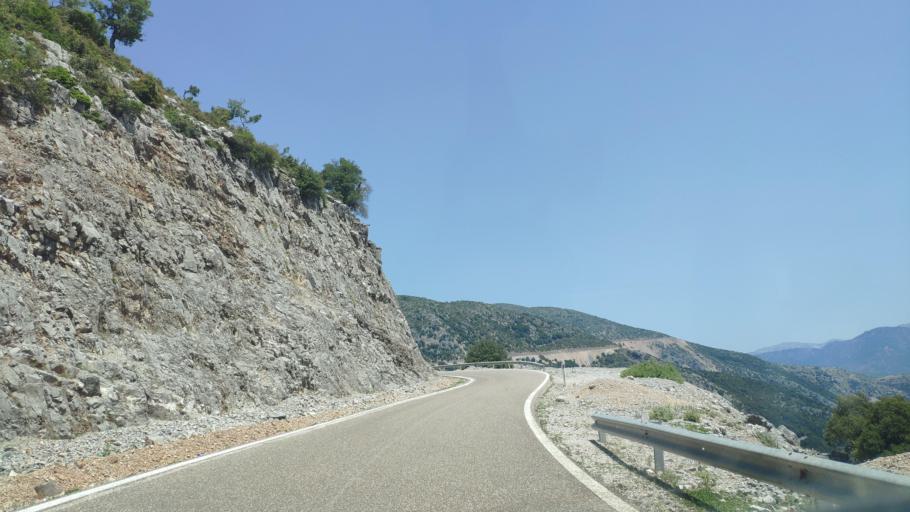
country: GR
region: West Greece
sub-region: Nomos Aitolias kai Akarnanias
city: Krikellos
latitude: 39.0233
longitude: 21.3704
